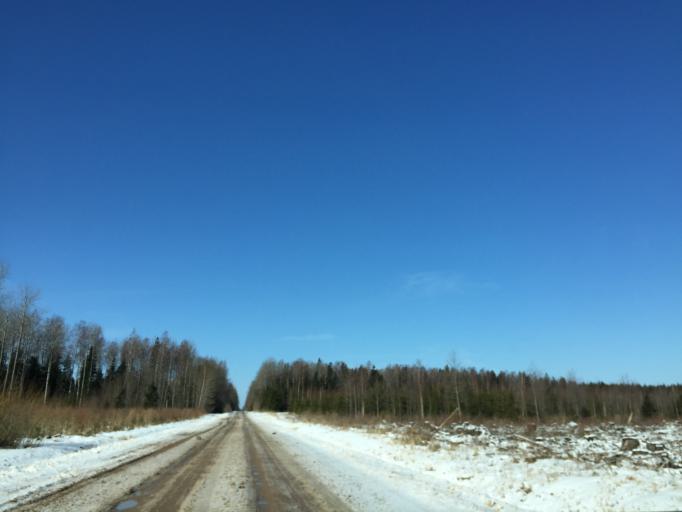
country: LV
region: Salacgrivas
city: Ainazi
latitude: 58.0276
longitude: 24.5609
